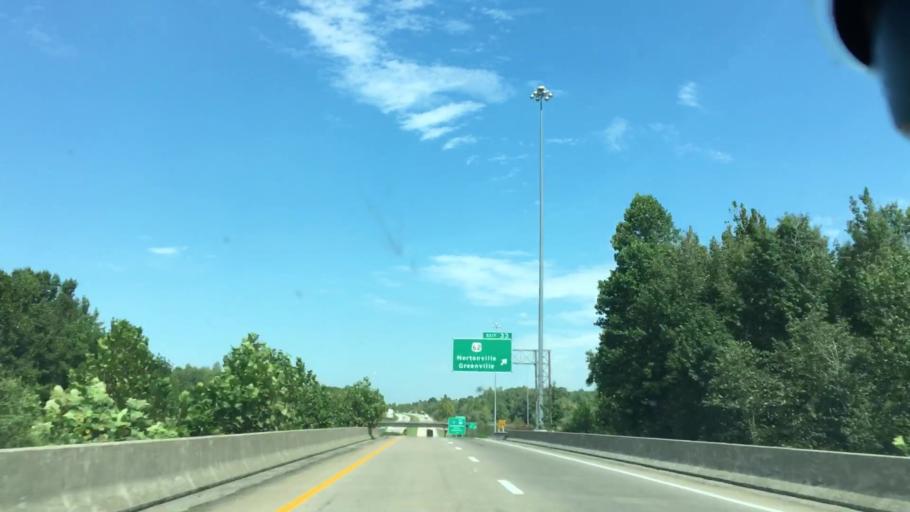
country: US
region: Kentucky
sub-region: Hopkins County
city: Nortonville
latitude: 37.1889
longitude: -87.4429
